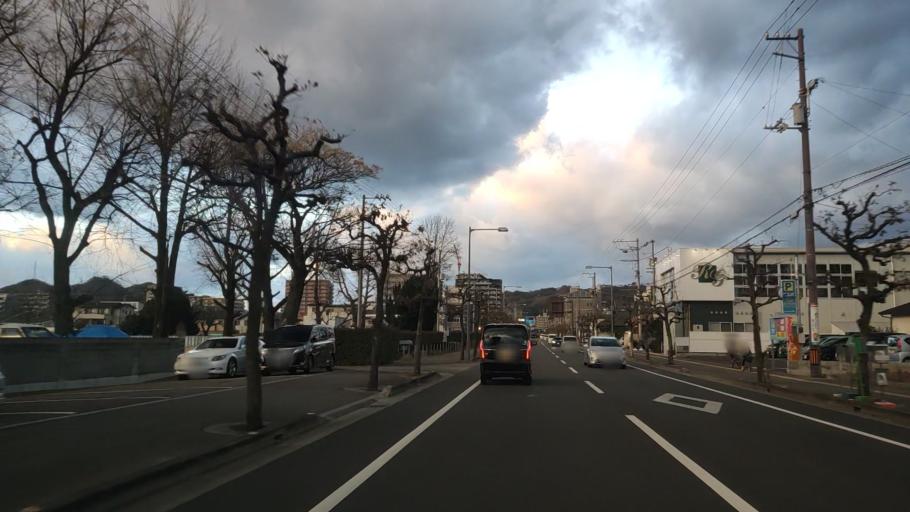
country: JP
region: Ehime
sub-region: Shikoku-chuo Shi
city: Matsuyama
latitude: 33.8428
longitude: 132.7844
